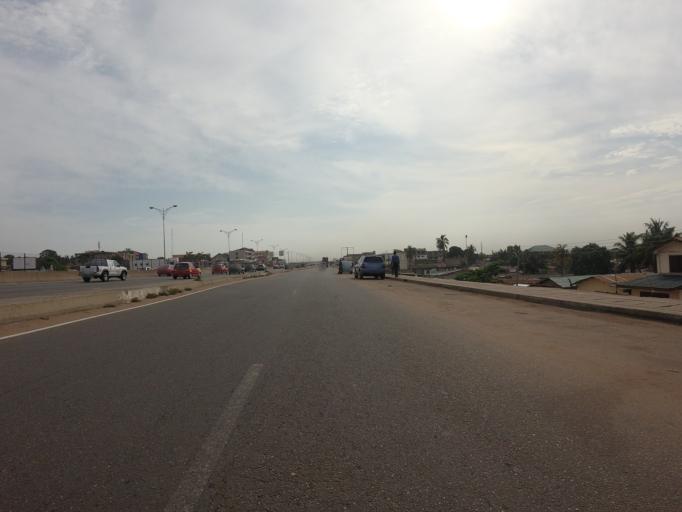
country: GH
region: Greater Accra
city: Dome
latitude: 5.6081
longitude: -0.2439
